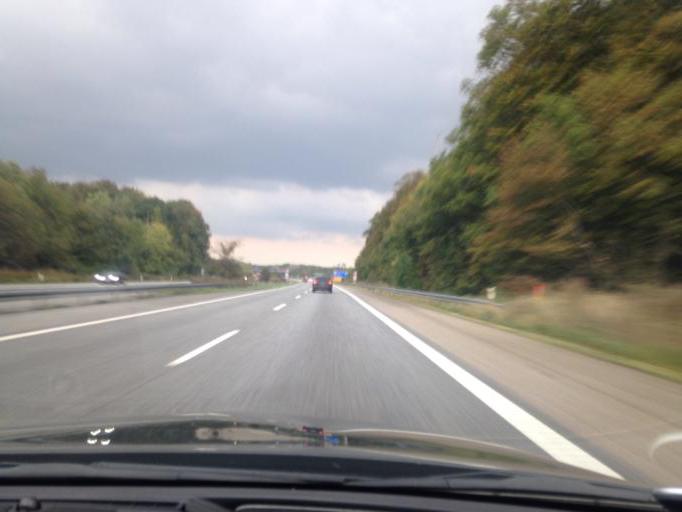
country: DK
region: South Denmark
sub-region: Kolding Kommune
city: Kolding
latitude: 55.4604
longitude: 9.4452
